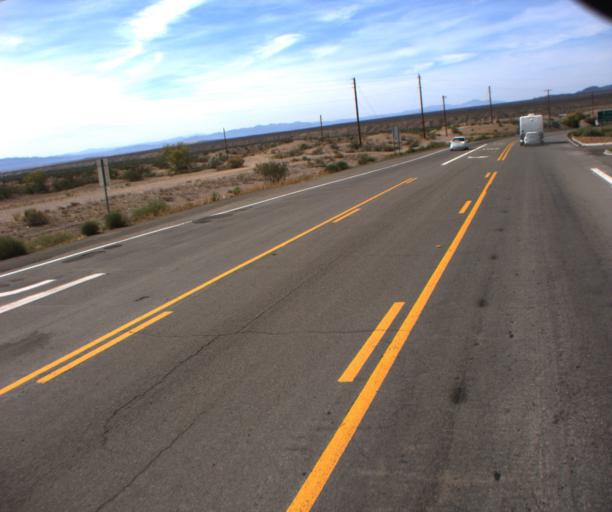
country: US
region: Arizona
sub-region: Mohave County
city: Desert Hills
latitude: 34.7262
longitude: -114.3157
